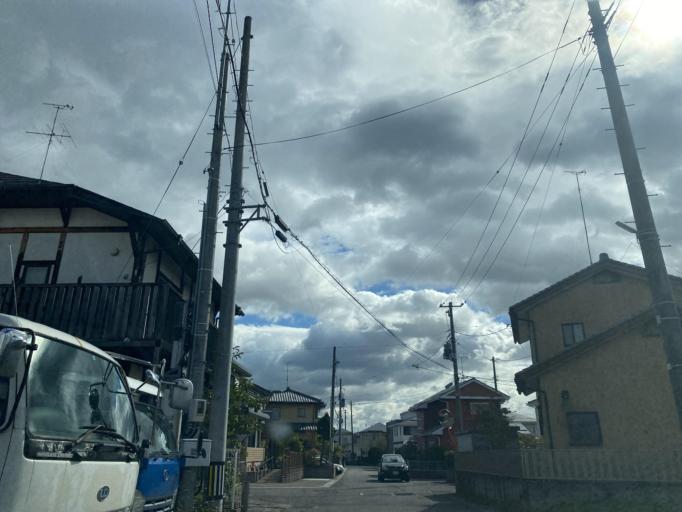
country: JP
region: Fukushima
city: Koriyama
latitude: 37.3834
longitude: 140.3402
